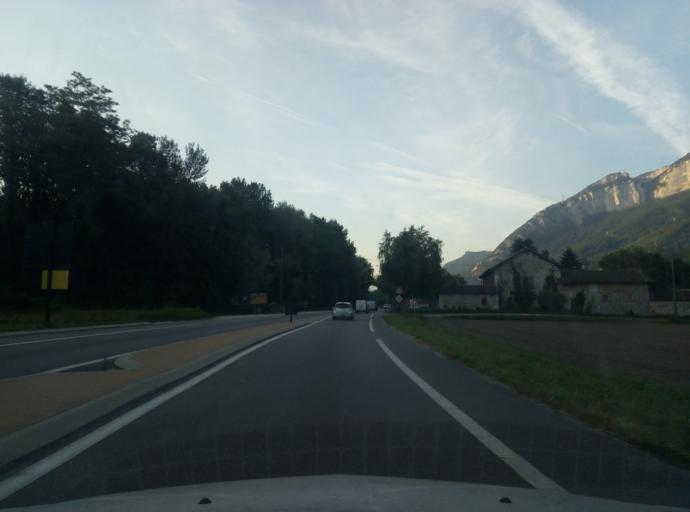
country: FR
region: Rhone-Alpes
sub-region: Departement de l'Isere
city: Veurey-Voroize
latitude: 45.2674
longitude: 5.6215
